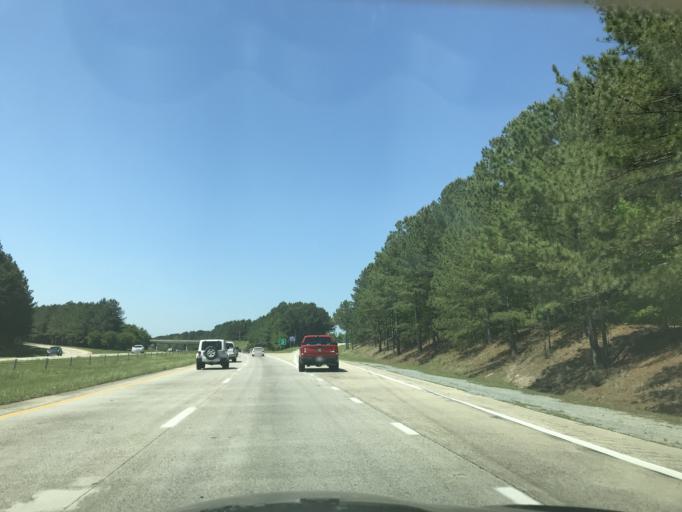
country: US
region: North Carolina
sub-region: Johnston County
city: Benson
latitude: 35.5128
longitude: -78.5561
